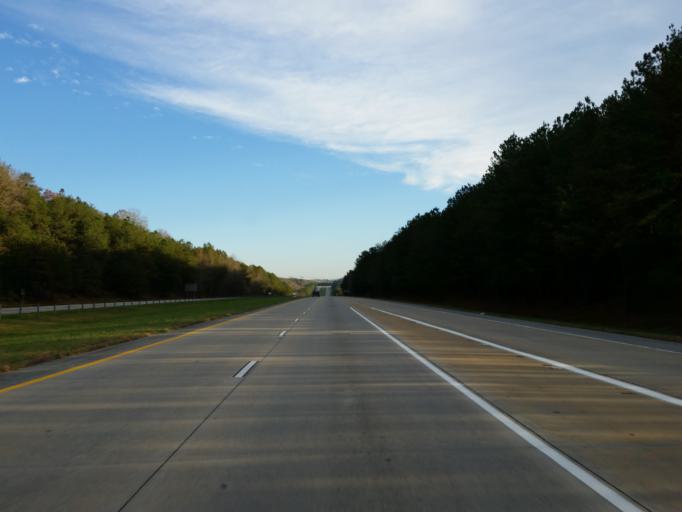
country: US
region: Georgia
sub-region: Cherokee County
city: Ball Ground
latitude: 34.3042
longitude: -84.4190
